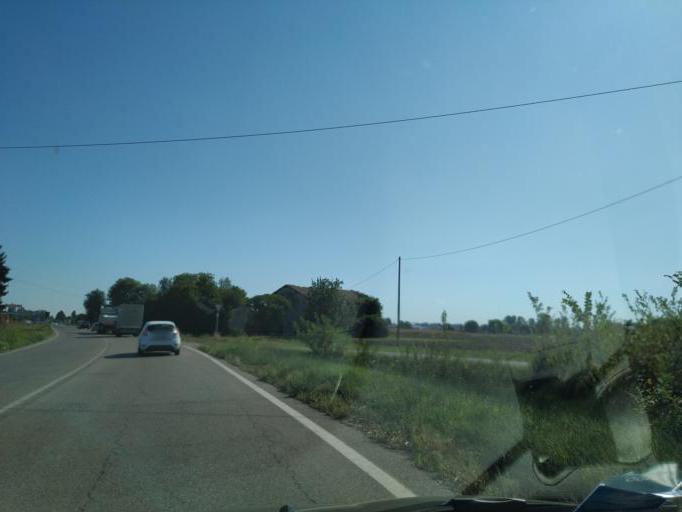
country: IT
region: Emilia-Romagna
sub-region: Provincia di Ferrara
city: Cento
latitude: 44.7443
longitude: 11.2864
